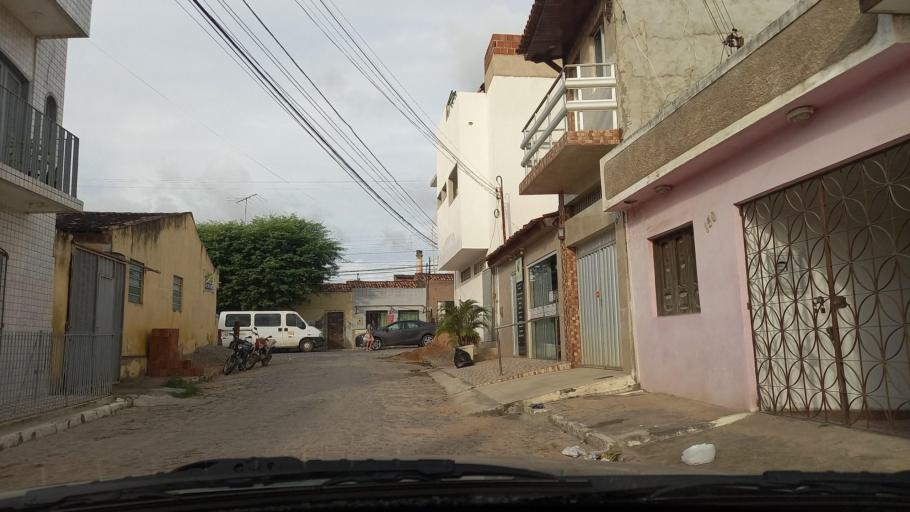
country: BR
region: Pernambuco
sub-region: Gravata
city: Gravata
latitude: -8.2047
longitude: -35.5635
